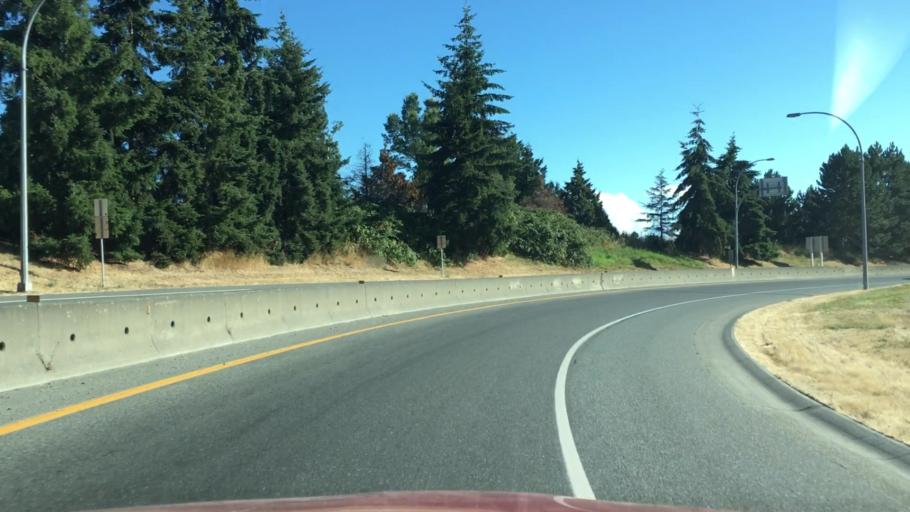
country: CA
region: British Columbia
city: Victoria
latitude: 48.4671
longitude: -123.3789
